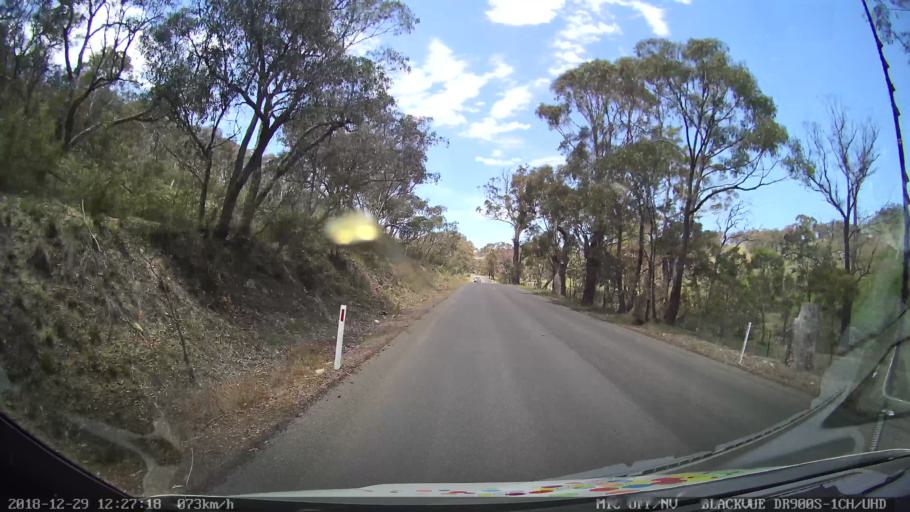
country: AU
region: Australian Capital Territory
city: Macarthur
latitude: -35.4752
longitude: 149.2231
